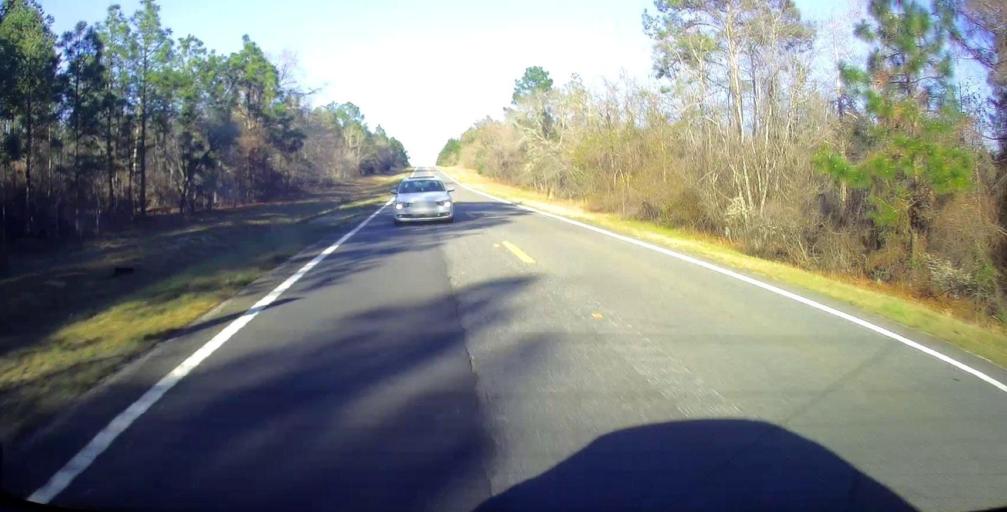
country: US
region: Georgia
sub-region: Taylor County
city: Butler
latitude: 32.5363
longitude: -84.2946
